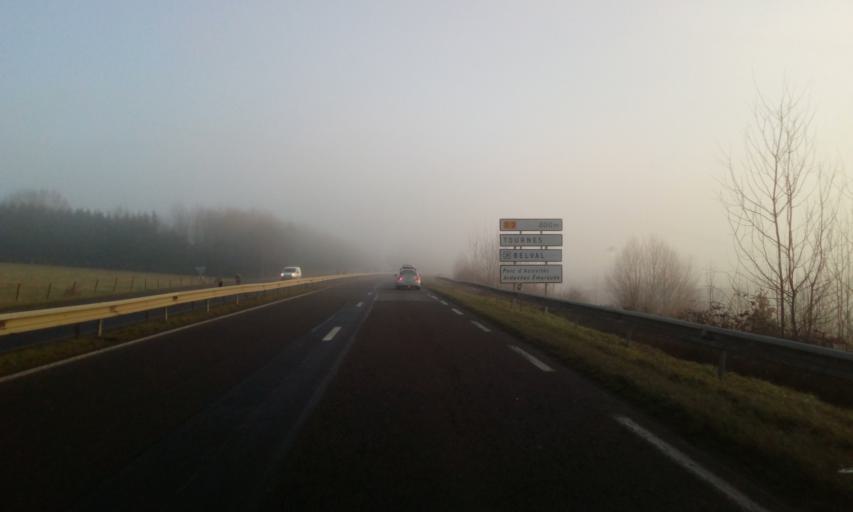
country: FR
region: Champagne-Ardenne
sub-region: Departement des Ardennes
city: Tournes
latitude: 49.8001
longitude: 4.6280
